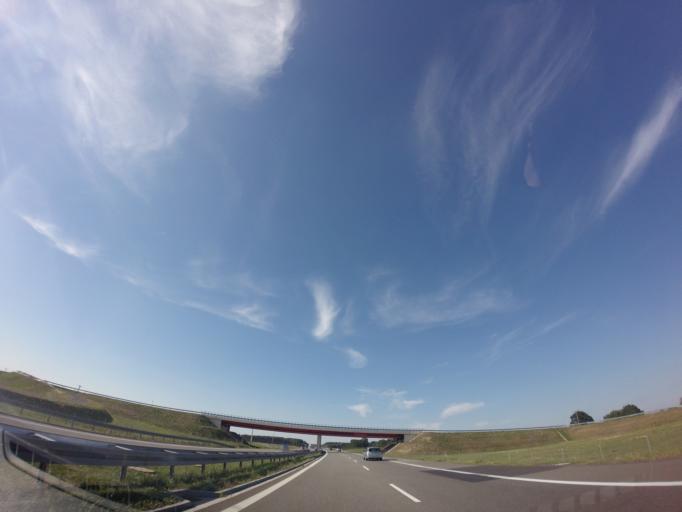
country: PL
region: Lubusz
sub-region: Powiat zielonogorski
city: Sulechow
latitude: 52.1650
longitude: 15.5877
